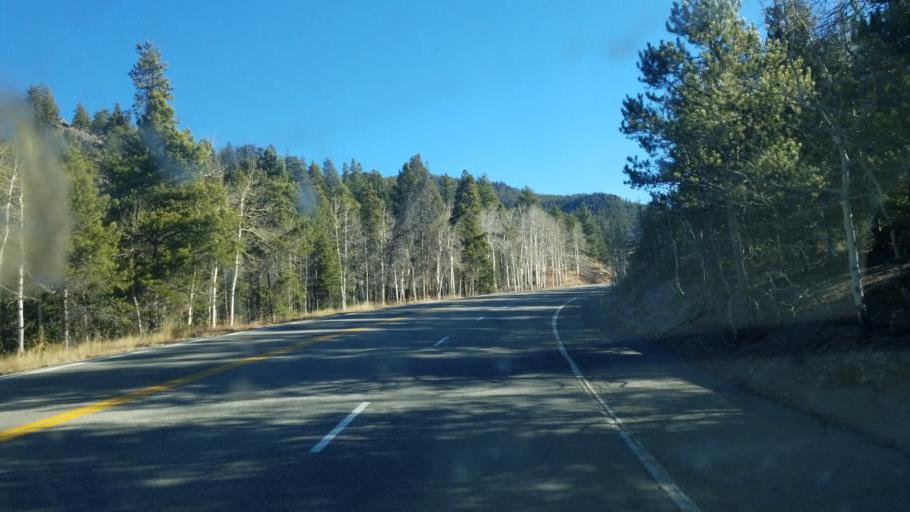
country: US
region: Colorado
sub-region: Chaffee County
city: Salida
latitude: 38.4388
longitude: -106.3830
